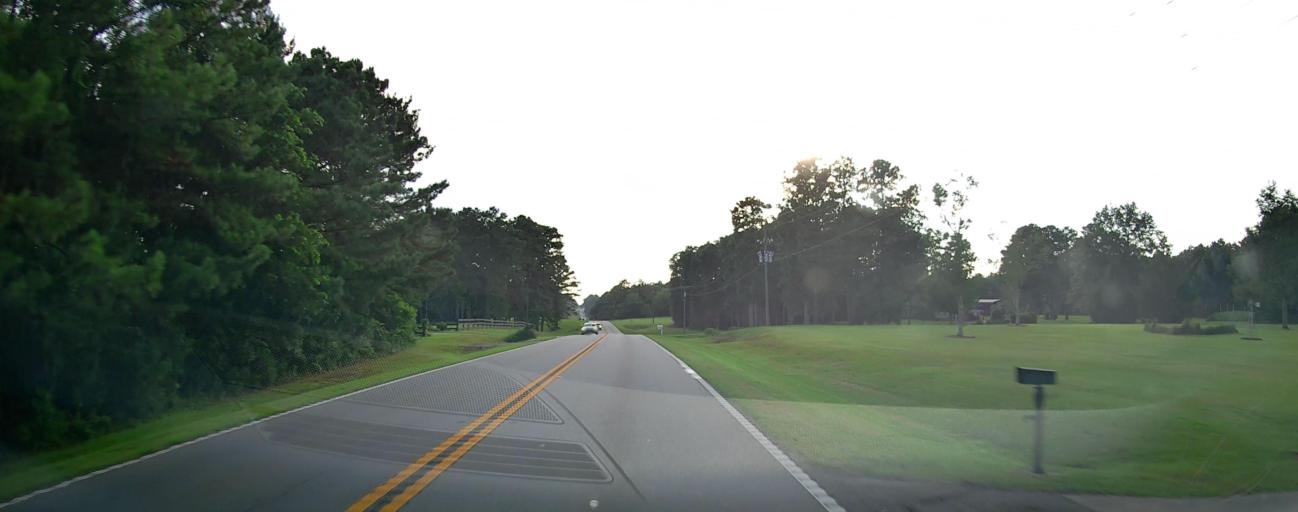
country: US
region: Georgia
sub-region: Peach County
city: Fort Valley
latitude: 32.5584
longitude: -83.9199
